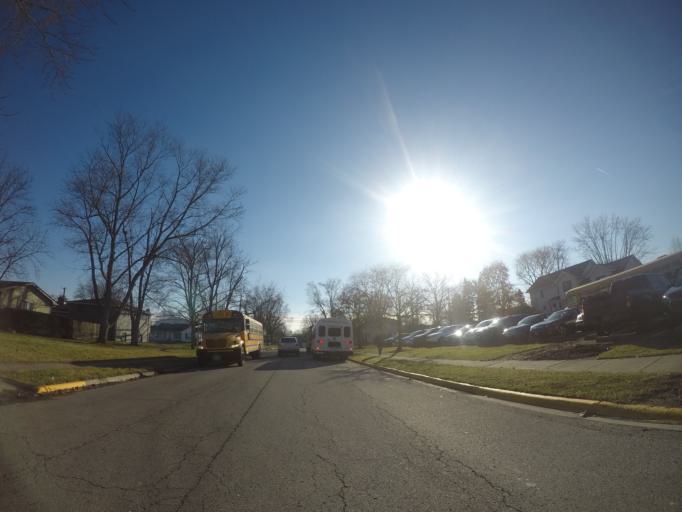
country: US
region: Ohio
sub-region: Franklin County
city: Upper Arlington
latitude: 40.0380
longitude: -83.0808
